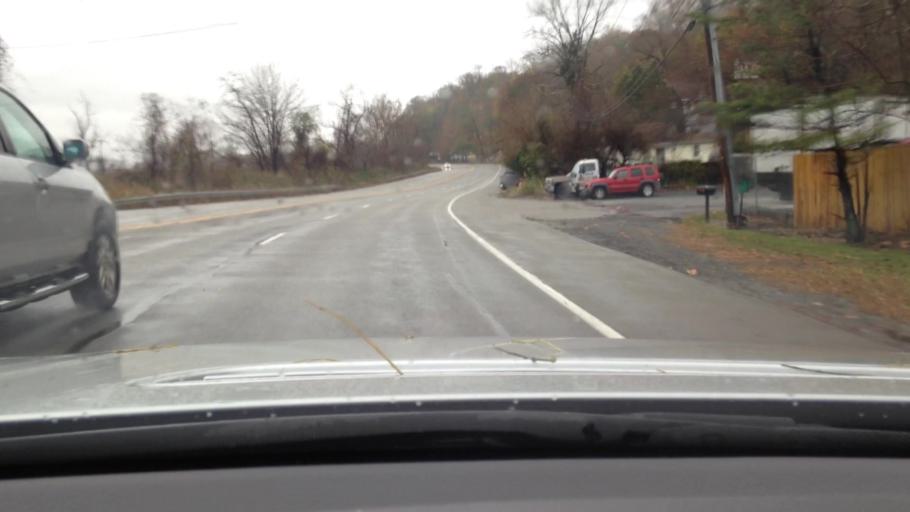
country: US
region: New York
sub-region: Westchester County
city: Peekskill
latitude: 41.3034
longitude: -73.9306
